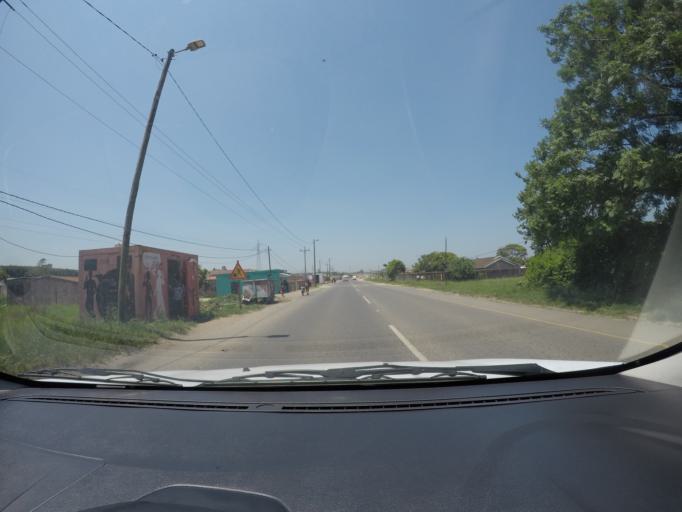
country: ZA
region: KwaZulu-Natal
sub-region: uThungulu District Municipality
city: eSikhawini
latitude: -28.8752
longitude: 31.8958
